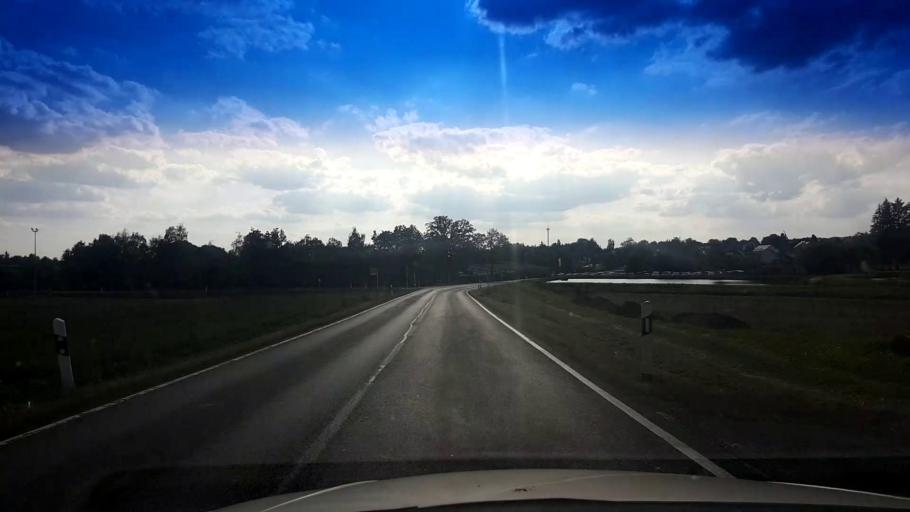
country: DE
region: Bavaria
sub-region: Upper Palatinate
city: Tirschenreuth
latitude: 49.8843
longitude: 12.3552
